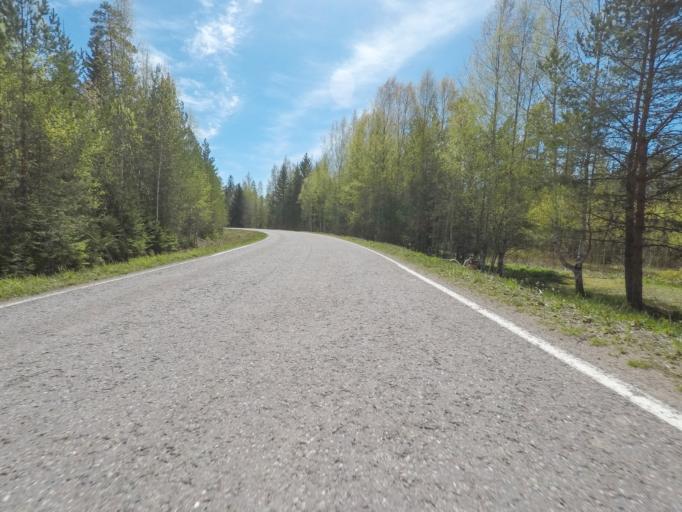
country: FI
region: Uusimaa
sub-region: Helsinki
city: Kaerkoelae
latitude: 60.5886
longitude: 23.7955
